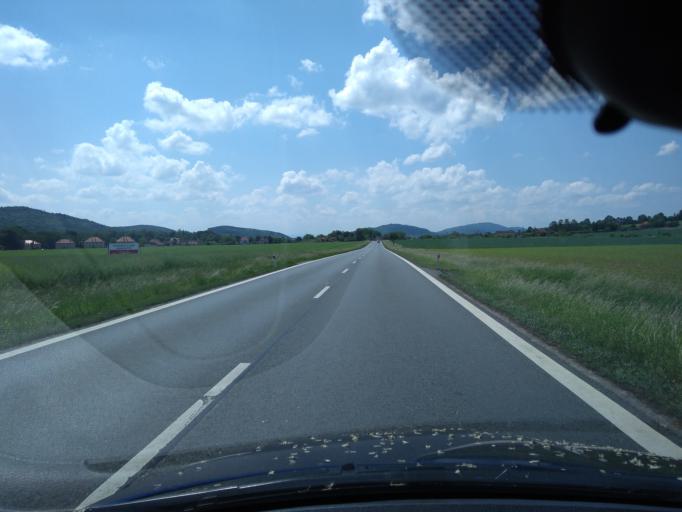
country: CZ
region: Plzensky
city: Prestice
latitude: 49.5554
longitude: 13.3183
